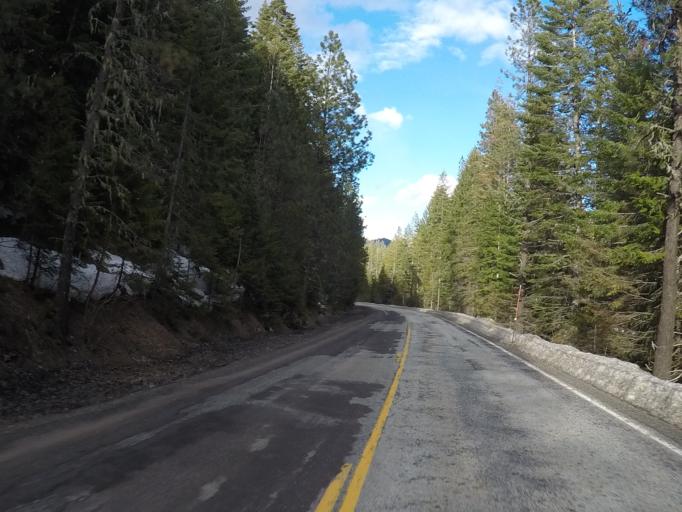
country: US
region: Montana
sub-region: Mineral County
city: Superior
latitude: 46.4938
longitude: -114.8669
